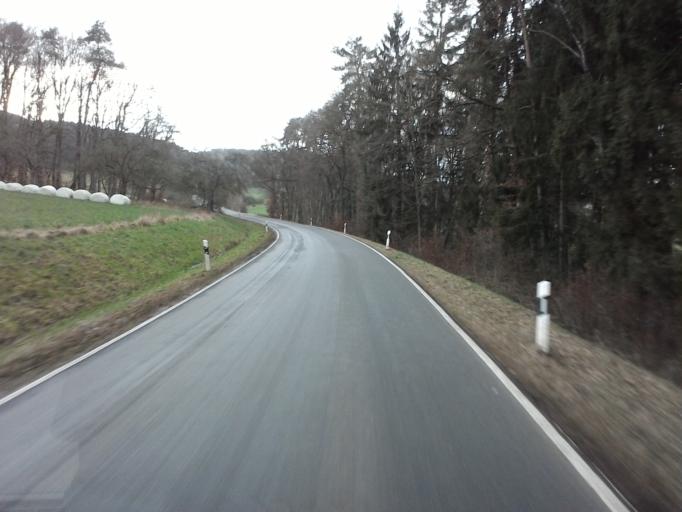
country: DE
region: Rheinland-Pfalz
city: Wettlingen
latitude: 49.9177
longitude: 6.3986
